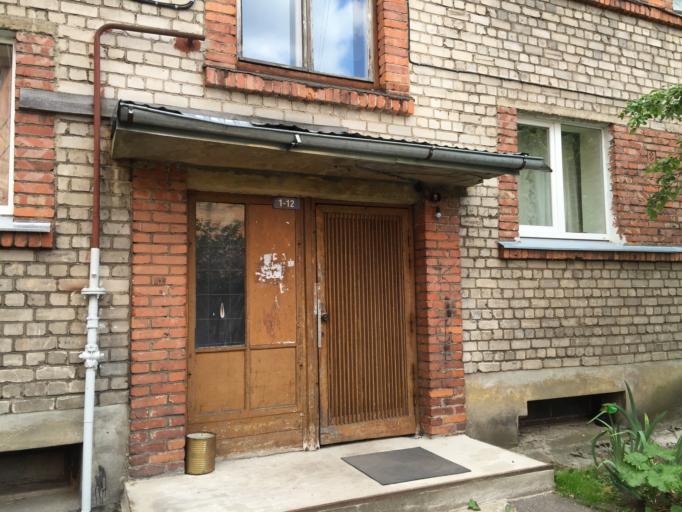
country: LV
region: Marupe
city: Marupe
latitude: 56.9399
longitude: 24.0647
